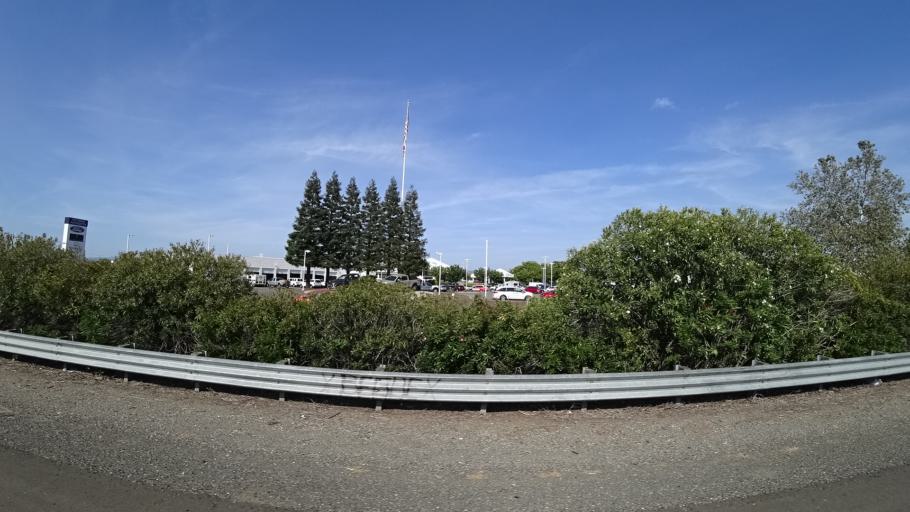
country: US
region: California
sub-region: Butte County
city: Chico
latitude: 39.7194
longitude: -121.8043
